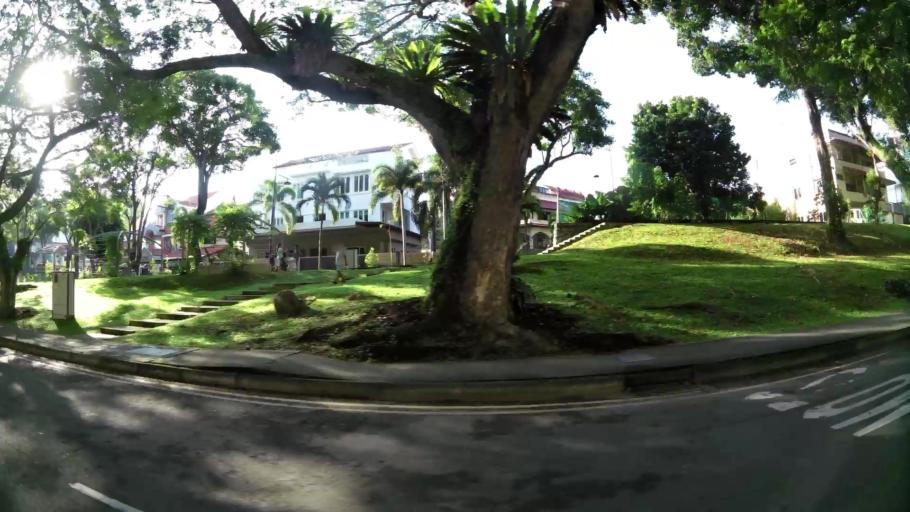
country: SG
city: Singapore
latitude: 1.3205
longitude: 103.9409
